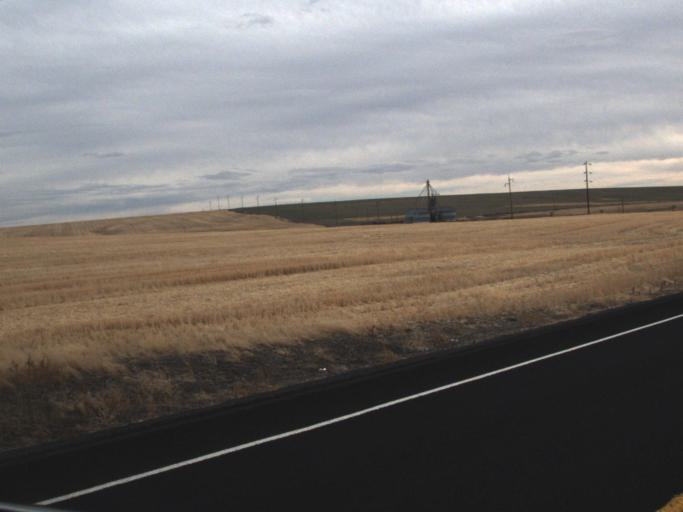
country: US
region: Washington
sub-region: Okanogan County
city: Coulee Dam
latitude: 47.7740
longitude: -118.7255
